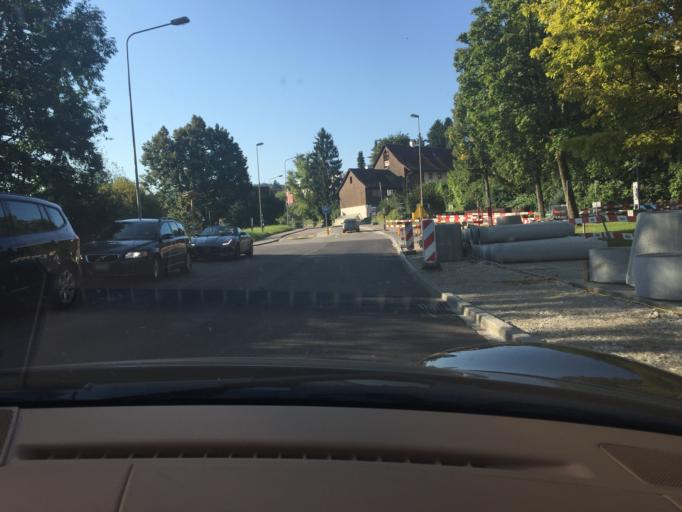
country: CH
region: Zurich
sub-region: Bezirk Uster
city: Aesch
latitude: 47.3310
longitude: 8.6547
